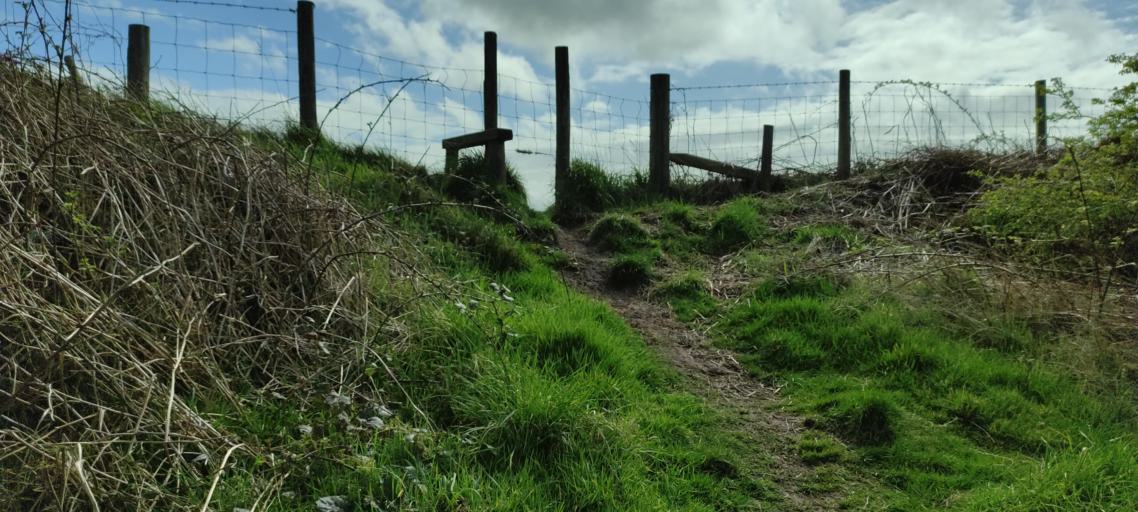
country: GB
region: England
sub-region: Cumbria
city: Maryport
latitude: 54.7281
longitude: -3.4850
